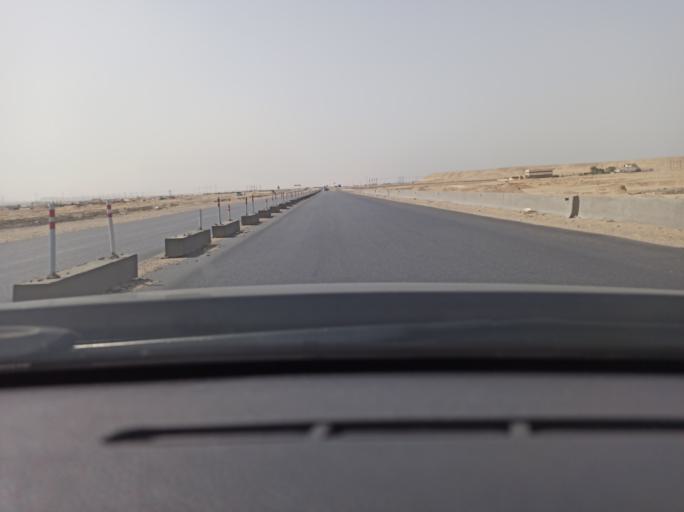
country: EG
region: Muhafazat al Fayyum
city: Al Wasitah
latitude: 29.2899
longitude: 31.2732
